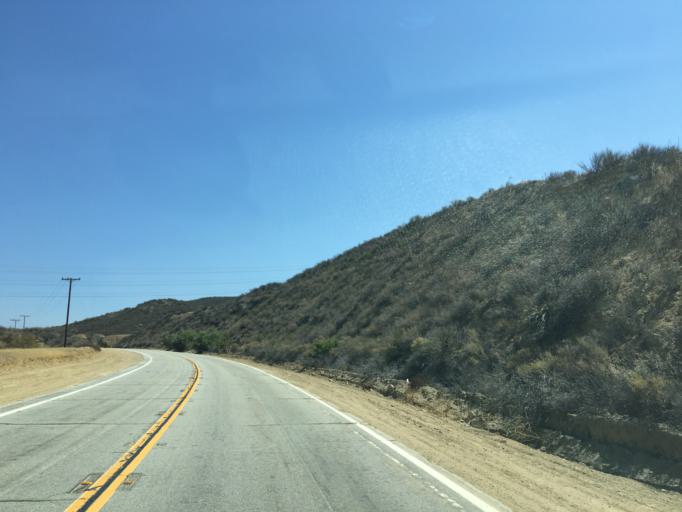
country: US
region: California
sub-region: Los Angeles County
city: Castaic
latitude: 34.5114
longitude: -118.5977
